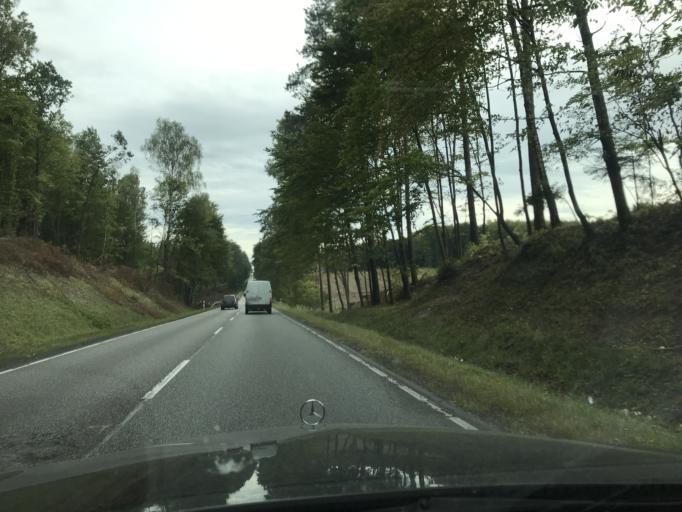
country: PL
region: Lublin Voivodeship
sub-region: Powiat krasnicki
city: Szastarka
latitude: 50.8563
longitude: 22.2839
